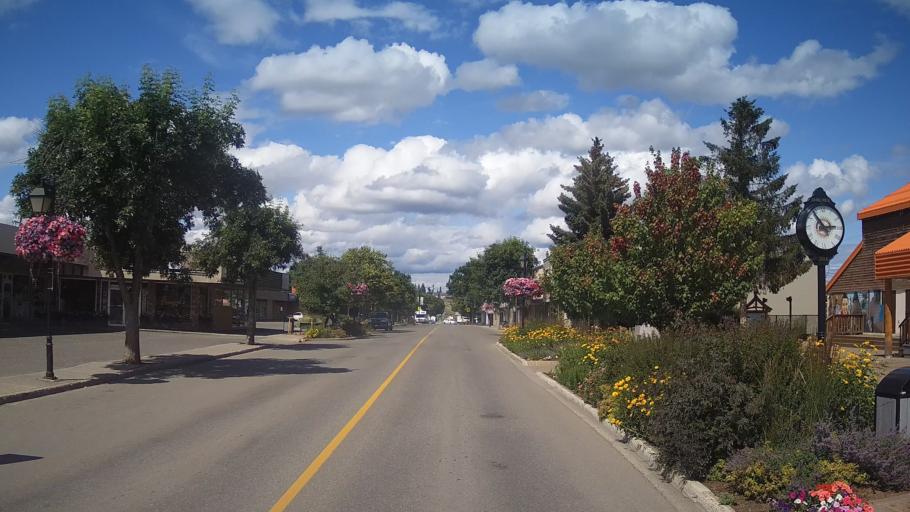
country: CA
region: British Columbia
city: Cache Creek
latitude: 51.6440
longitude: -121.2956
